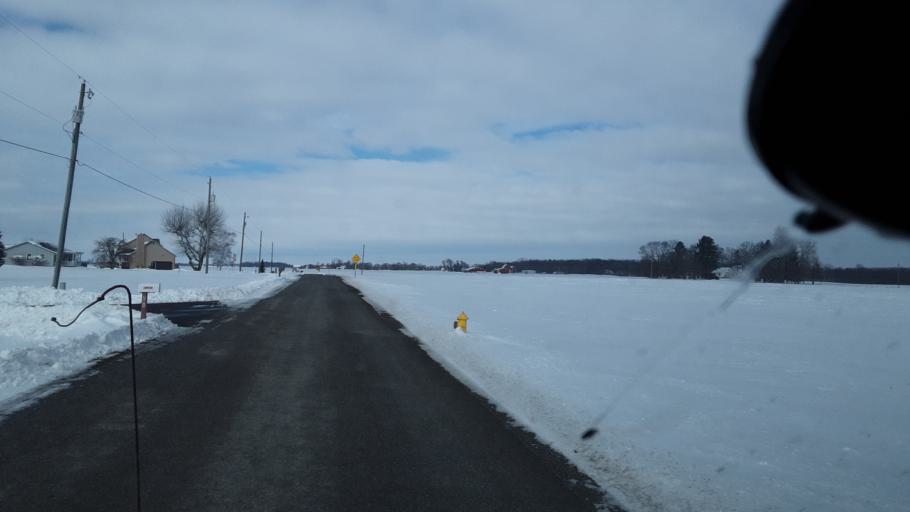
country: US
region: Ohio
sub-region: Delaware County
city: Delaware
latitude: 40.2850
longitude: -82.9911
